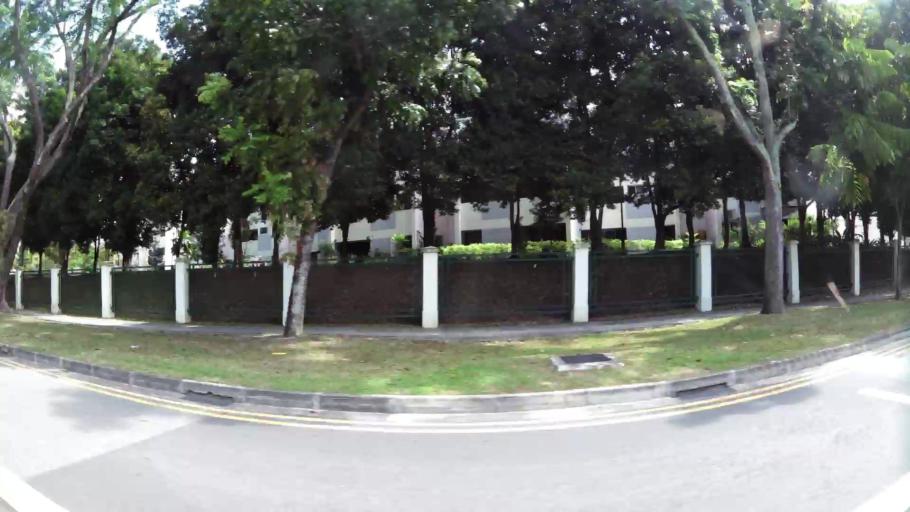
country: SG
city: Singapore
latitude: 1.3360
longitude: 103.7353
